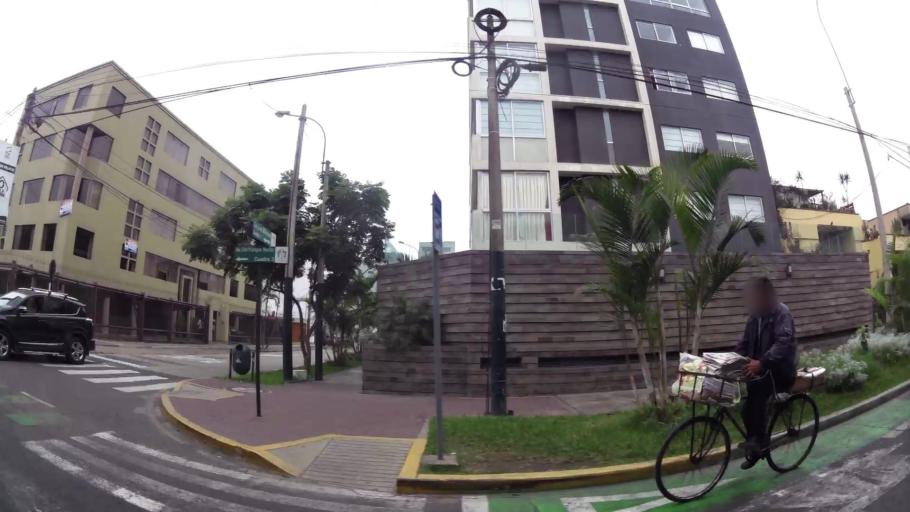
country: PE
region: Lima
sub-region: Lima
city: San Luis
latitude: -12.0924
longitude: -77.0182
